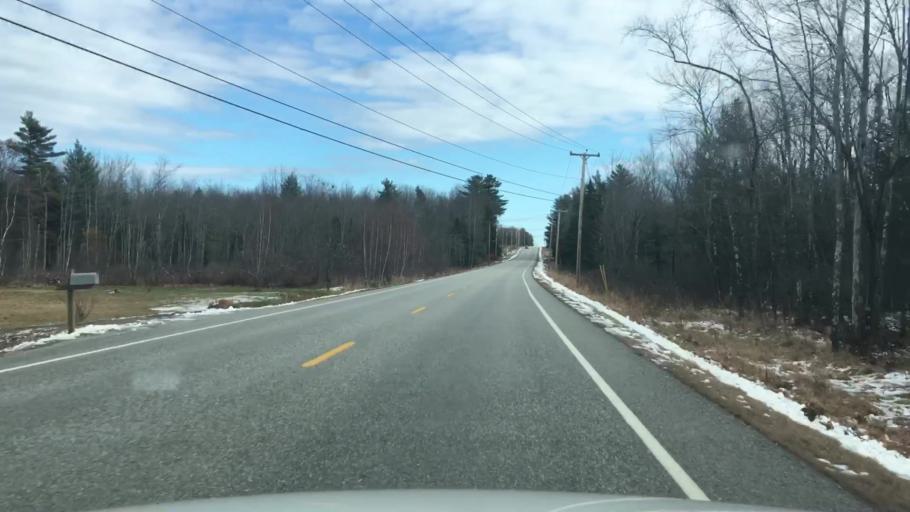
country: US
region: Maine
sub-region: Androscoggin County
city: Leeds
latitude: 44.3430
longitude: -70.1785
